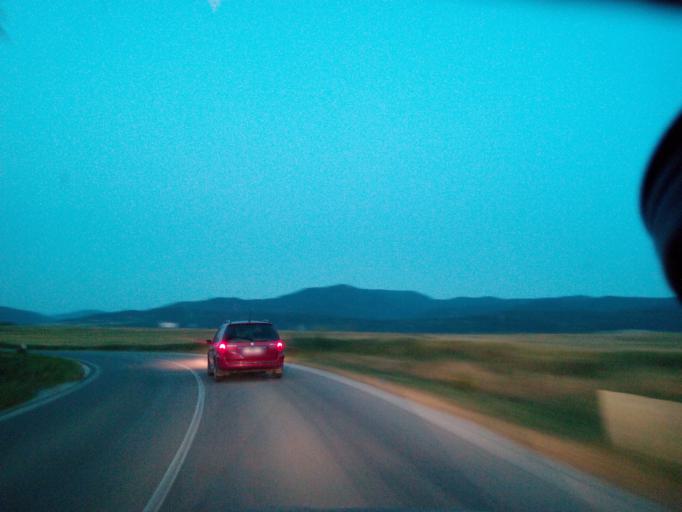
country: SK
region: Presovsky
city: Spisske Podhradie
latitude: 48.9454
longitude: 20.7694
